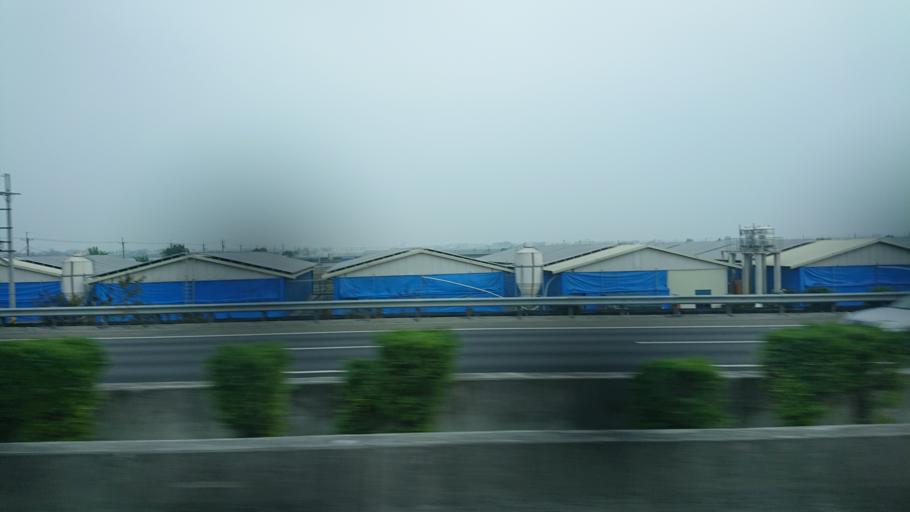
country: TW
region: Taiwan
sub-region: Yunlin
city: Douliu
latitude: 23.7628
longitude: 120.4684
